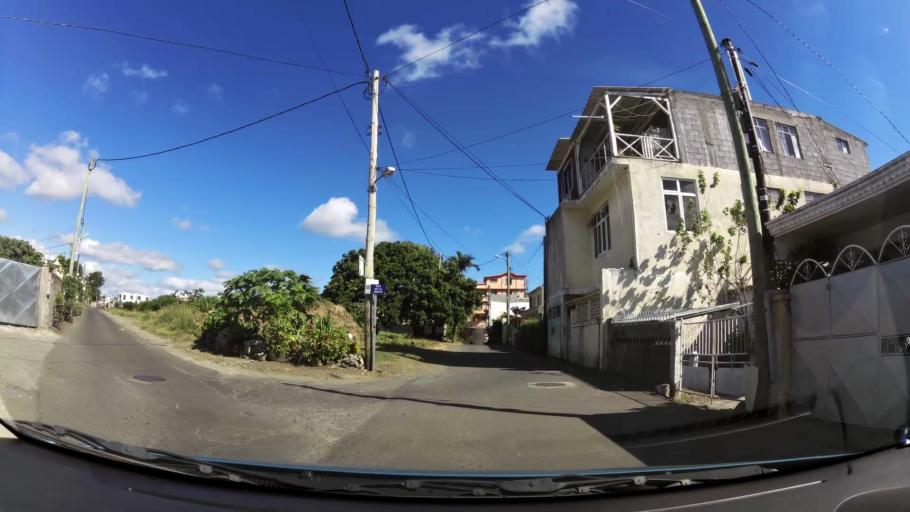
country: MU
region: Plaines Wilhems
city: Quatre Bornes
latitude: -20.2804
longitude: 57.4733
